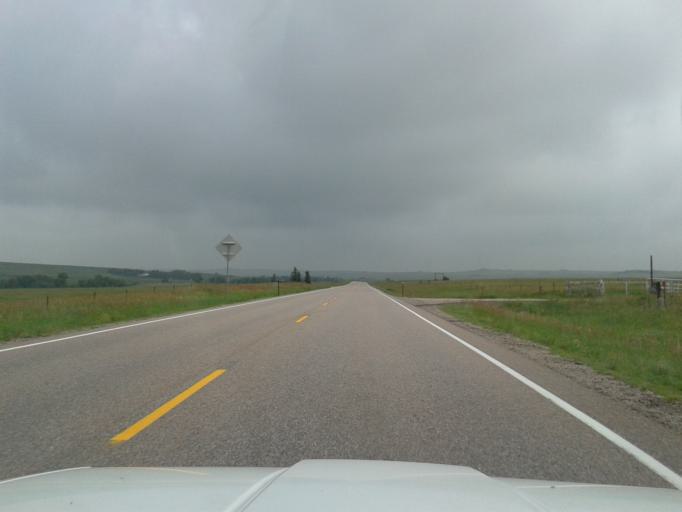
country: US
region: Colorado
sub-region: El Paso County
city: Woodmoor
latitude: 39.2100
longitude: -104.7122
